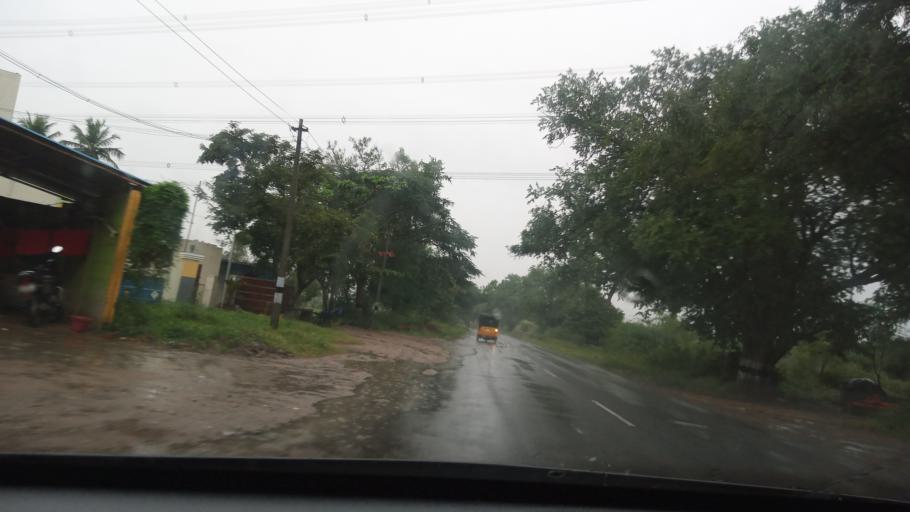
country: IN
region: Tamil Nadu
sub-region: Vellore
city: Walajapet
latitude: 12.8574
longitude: 79.3805
